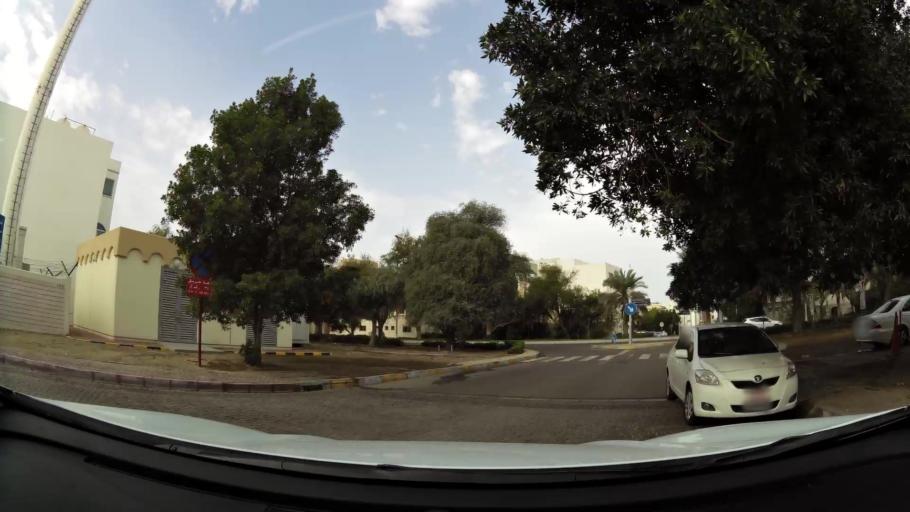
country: AE
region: Abu Dhabi
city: Abu Dhabi
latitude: 24.4435
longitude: 54.4086
